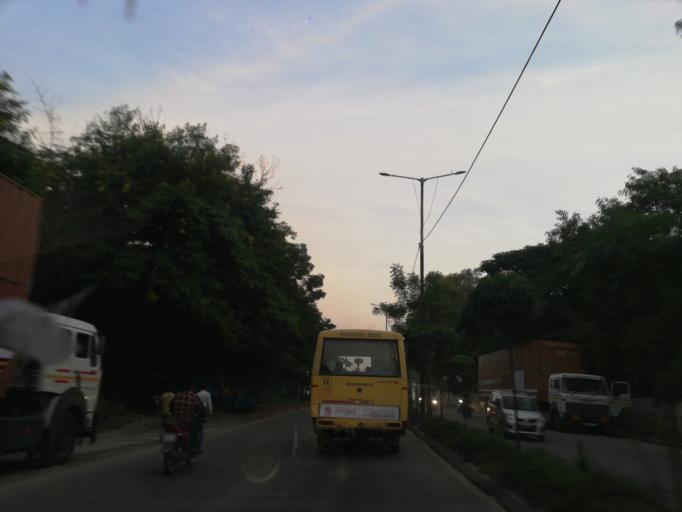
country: IN
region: Telangana
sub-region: Rangareddi
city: Kukatpalli
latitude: 17.5108
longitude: 78.3616
